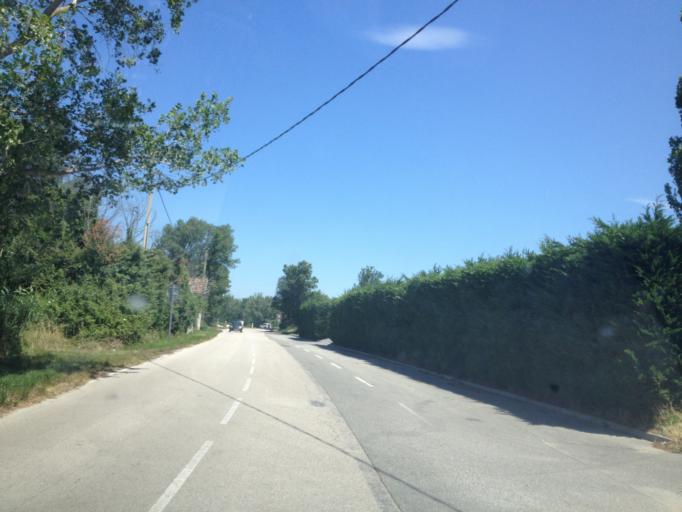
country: FR
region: Provence-Alpes-Cote d'Azur
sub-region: Departement du Vaucluse
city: Sorgues
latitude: 44.0235
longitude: 4.8820
